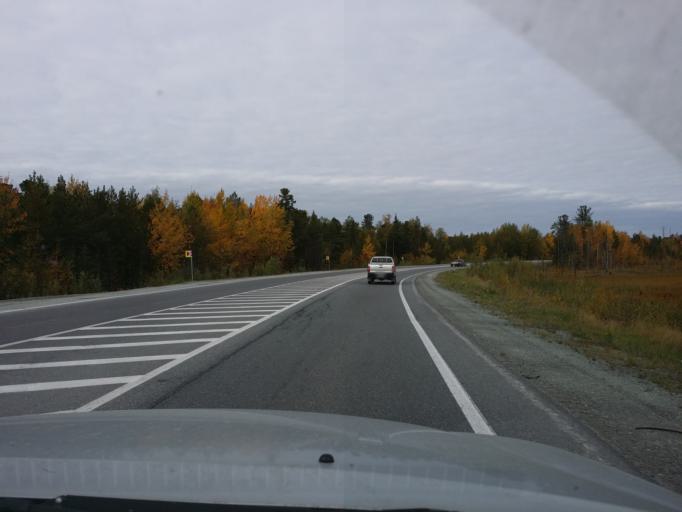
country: RU
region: Khanty-Mansiyskiy Avtonomnyy Okrug
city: Megion
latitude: 61.1003
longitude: 75.8608
